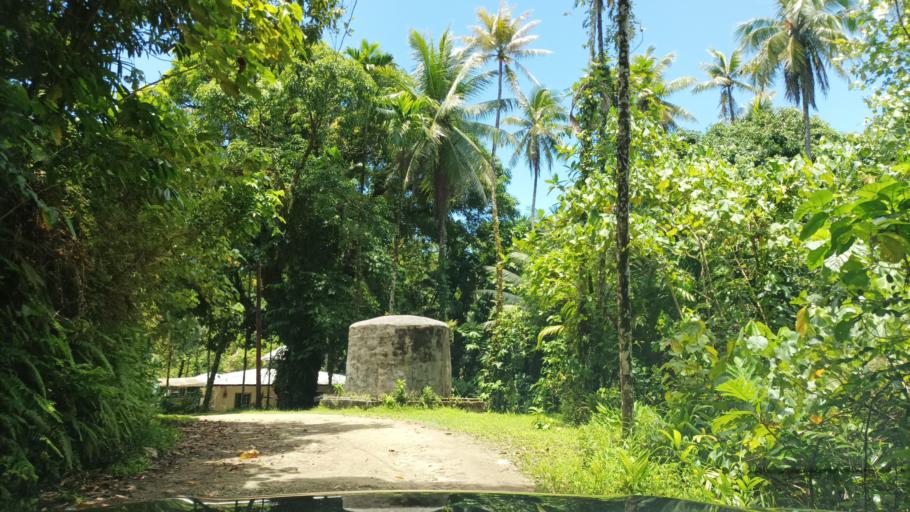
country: FM
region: Pohnpei
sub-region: Madolenihm Municipality
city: Madolenihm Municipality Government
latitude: 6.8446
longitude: 158.3175
